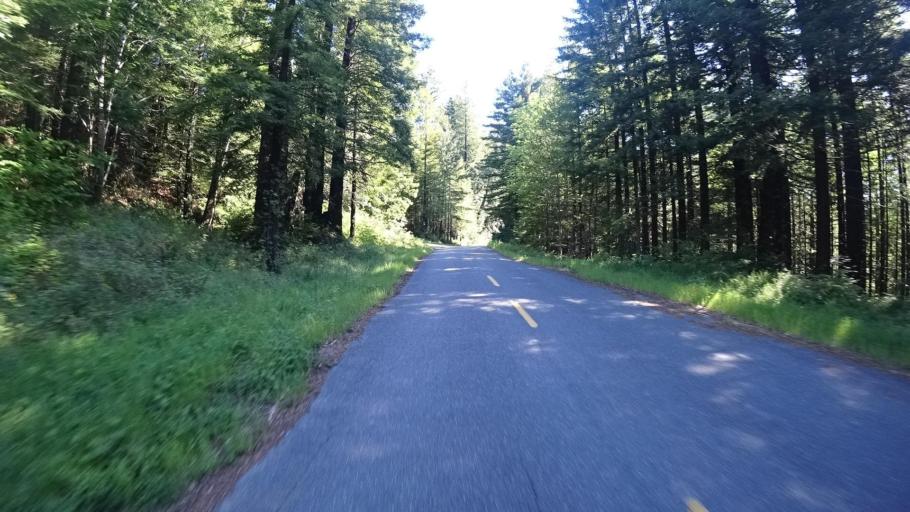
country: US
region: California
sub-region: Humboldt County
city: Rio Dell
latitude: 40.4593
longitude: -124.0653
